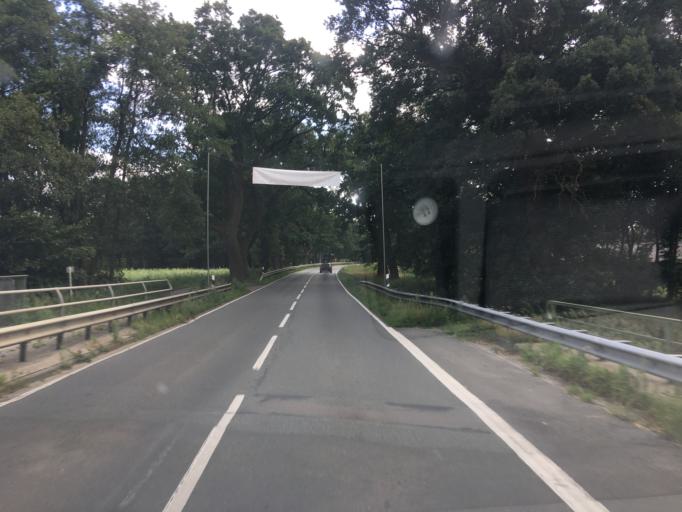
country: DE
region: Lower Saxony
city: Friesoythe
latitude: 53.0693
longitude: 7.8472
